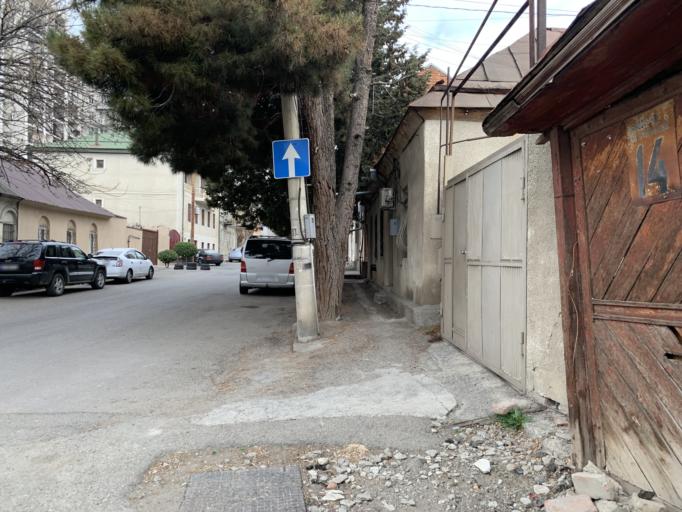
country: GE
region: T'bilisi
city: Tbilisi
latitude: 41.6796
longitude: 44.8390
